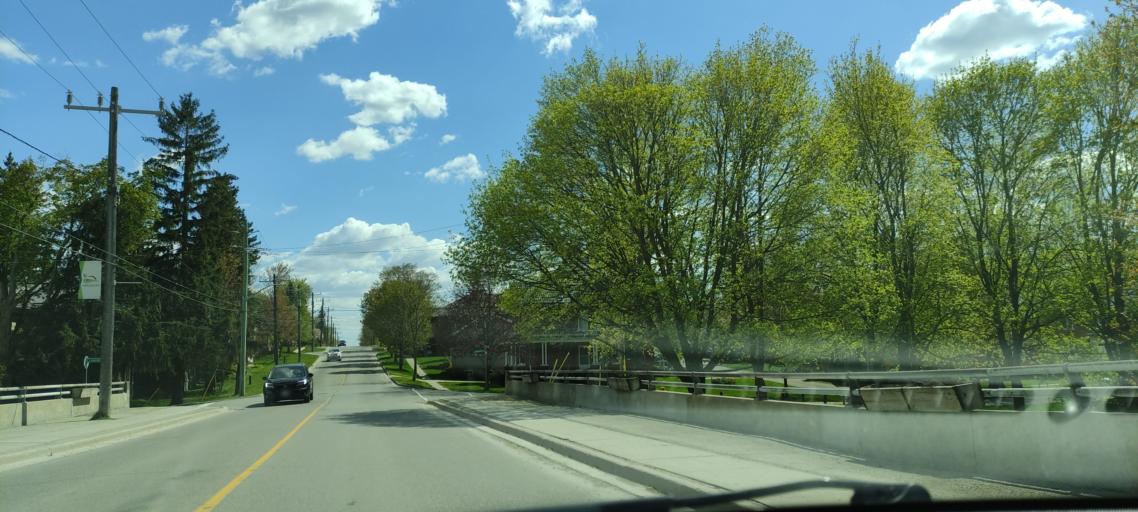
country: CA
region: Ontario
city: Stratford
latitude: 43.4752
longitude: -80.7645
